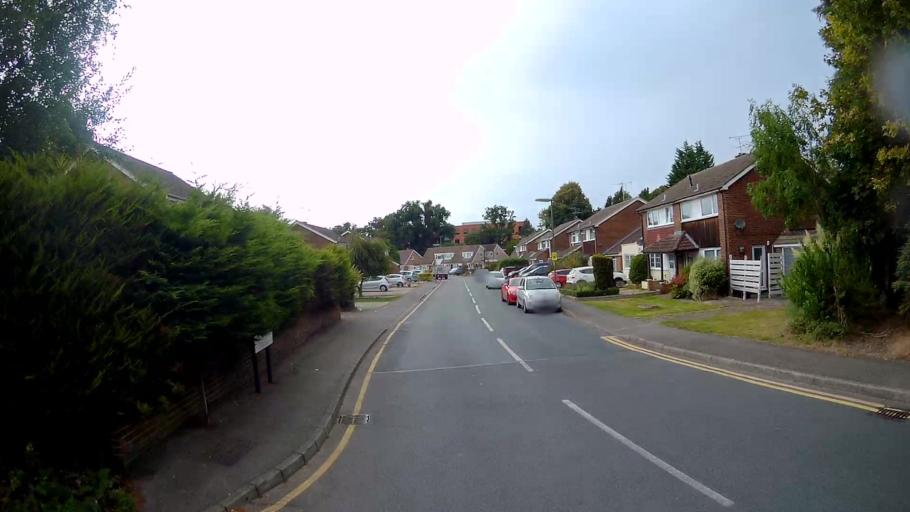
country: GB
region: England
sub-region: Surrey
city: Frimley
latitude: 51.3162
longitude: -0.7338
